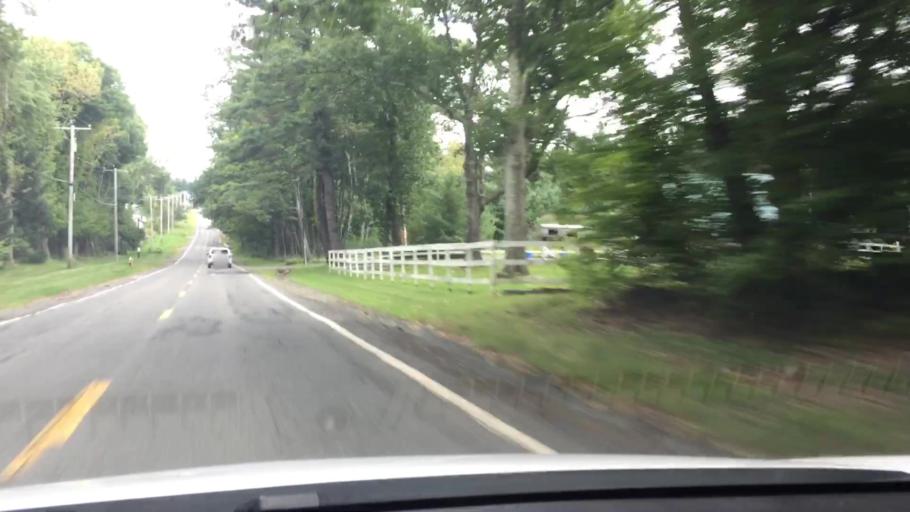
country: US
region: Massachusetts
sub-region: Hampden County
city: Granville
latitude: 42.1869
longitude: -72.9316
